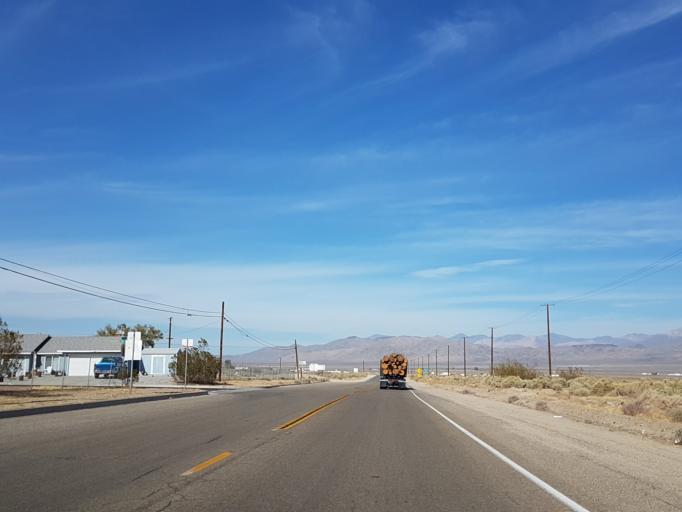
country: US
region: California
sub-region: San Bernardino County
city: Searles Valley
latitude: 35.7943
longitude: -117.3559
